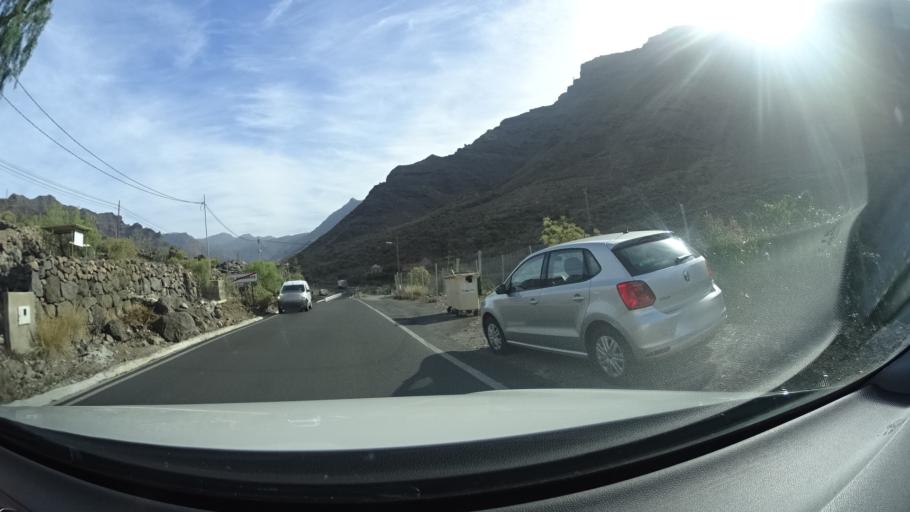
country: ES
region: Canary Islands
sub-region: Provincia de Las Palmas
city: Mogan
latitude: 27.8645
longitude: -15.7412
